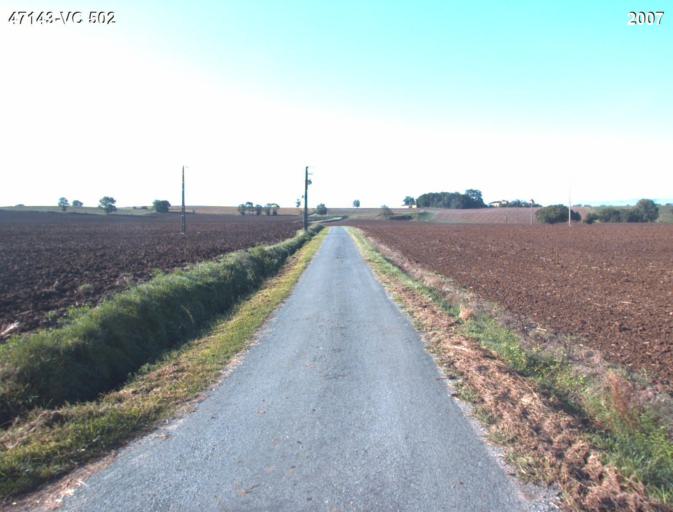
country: FR
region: Aquitaine
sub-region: Departement du Lot-et-Garonne
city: Vianne
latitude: 44.1809
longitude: 0.3300
